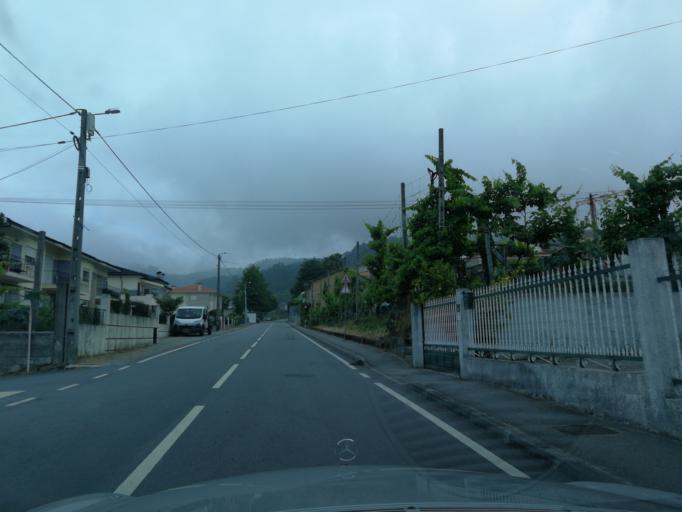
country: PT
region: Braga
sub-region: Guimaraes
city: Ponte
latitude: 41.5141
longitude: -8.3560
